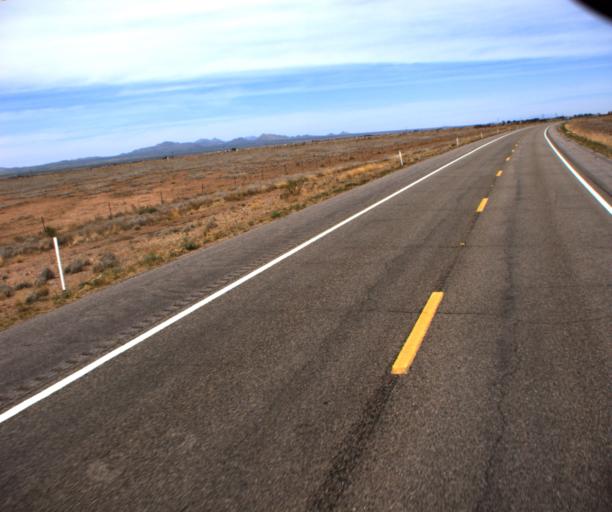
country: US
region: Arizona
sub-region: Cochise County
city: Pirtleville
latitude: 31.5621
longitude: -109.6672
